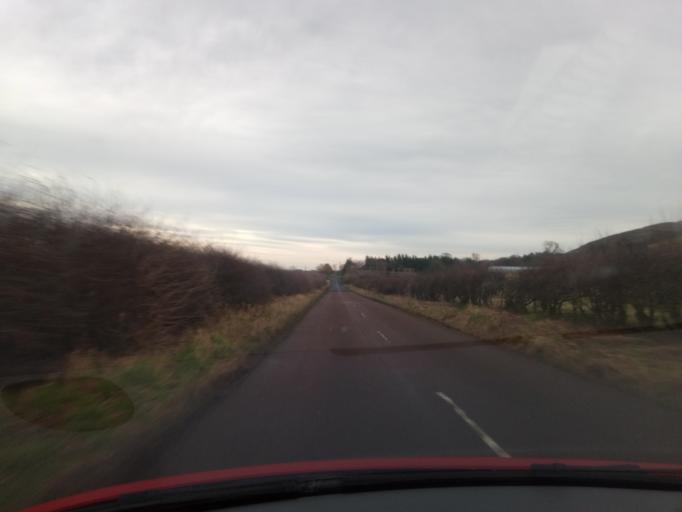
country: GB
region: England
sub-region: Northumberland
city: Kirknewton
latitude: 55.5617
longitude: -2.0749
